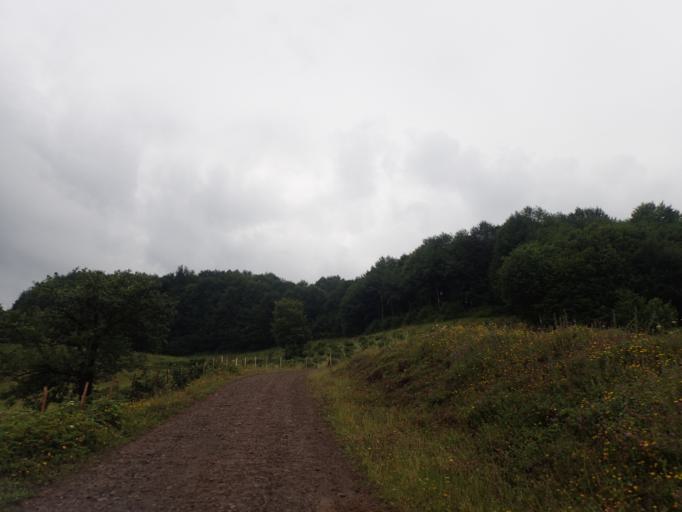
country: TR
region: Ordu
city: Akkus
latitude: 40.8082
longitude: 37.1107
